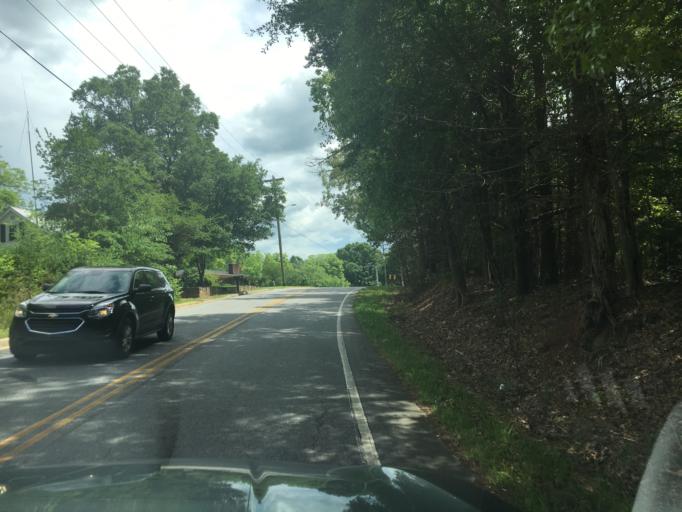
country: US
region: South Carolina
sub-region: Spartanburg County
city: Duncan
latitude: 34.8651
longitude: -82.1145
